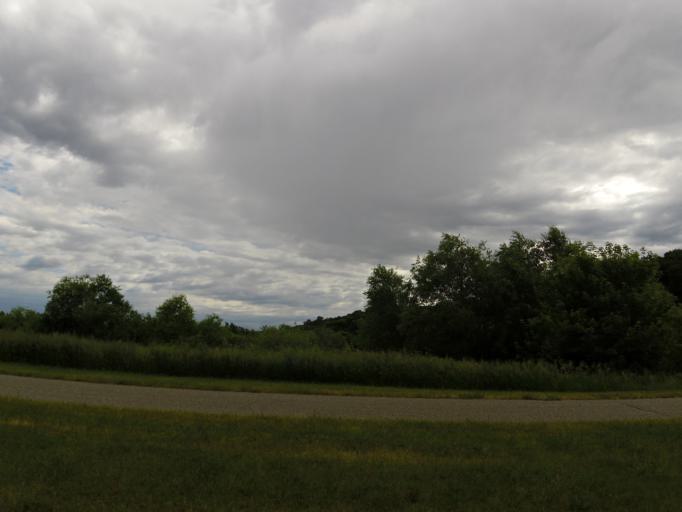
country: US
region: Minnesota
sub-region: Scott County
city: Prior Lake
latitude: 44.7581
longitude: -93.4444
